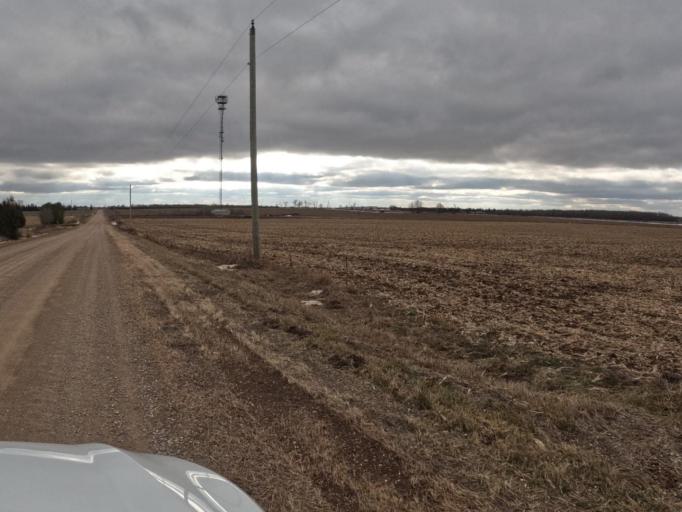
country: CA
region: Ontario
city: Shelburne
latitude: 43.8713
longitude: -80.3787
